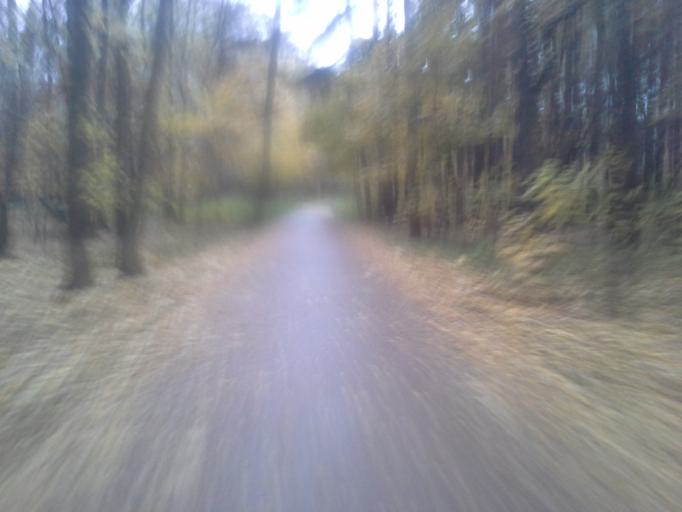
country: RU
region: Moskovskaya
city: Skolkovo
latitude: 55.6620
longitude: 37.3721
